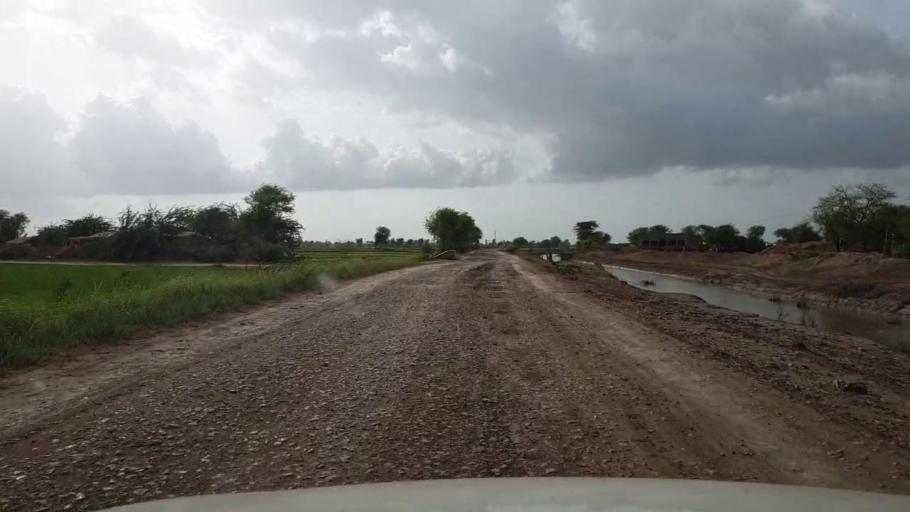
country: PK
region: Sindh
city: Kario
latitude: 24.7883
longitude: 68.5822
